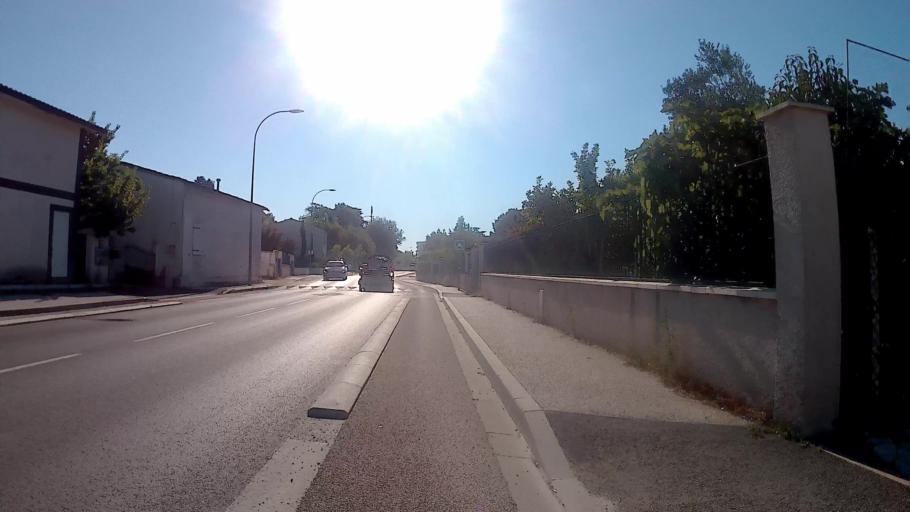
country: FR
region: Aquitaine
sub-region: Departement de la Gironde
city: Villenave-d'Ornon
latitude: 44.7814
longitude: -0.5623
